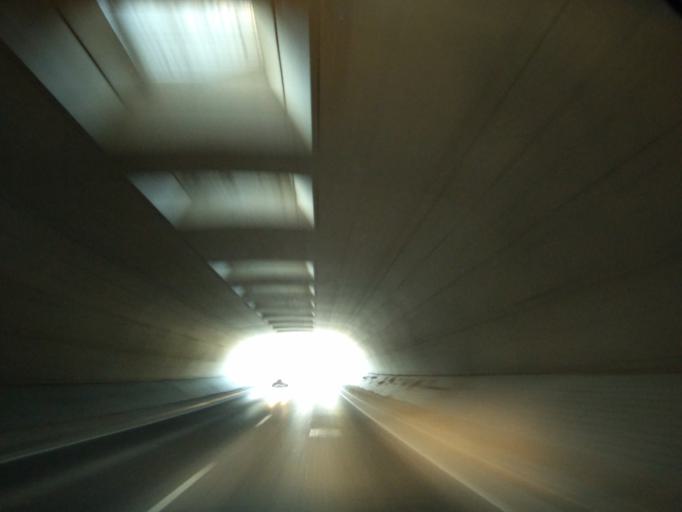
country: DE
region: Baden-Wuerttemberg
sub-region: Regierungsbezirk Stuttgart
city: Bietigheim-Bissingen
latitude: 48.9532
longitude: 9.1160
